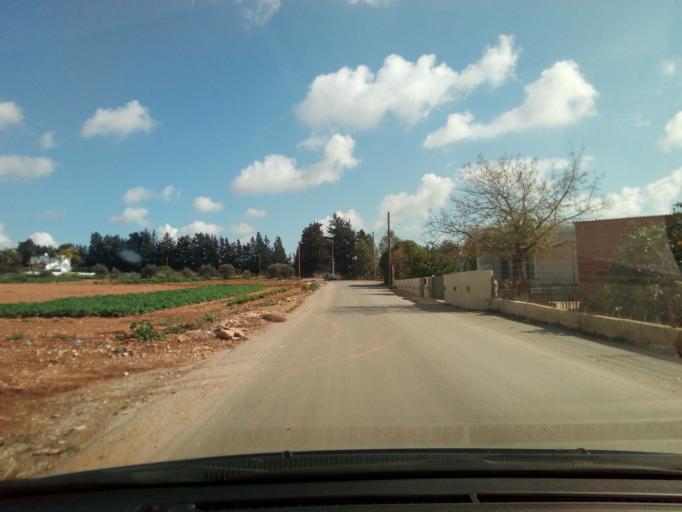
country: CY
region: Pafos
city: Empa
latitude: 34.8058
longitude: 32.4331
